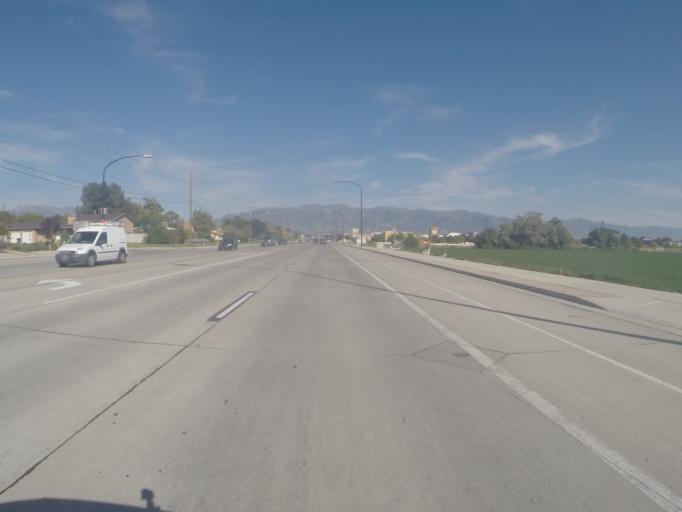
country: US
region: Utah
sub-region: Davis County
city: Syracuse
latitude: 41.0891
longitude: -112.0517
